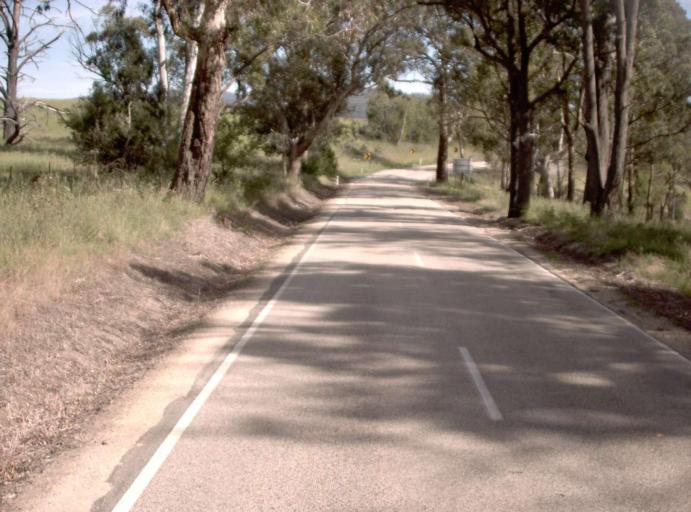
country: AU
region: Victoria
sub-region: East Gippsland
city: Lakes Entrance
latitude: -37.5199
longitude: 148.1622
